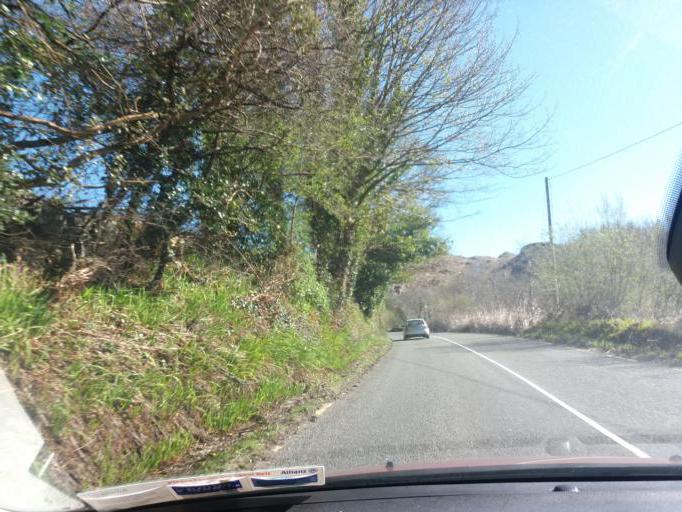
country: IE
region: Munster
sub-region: Ciarrai
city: Cill Airne
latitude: 51.9210
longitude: -9.3872
